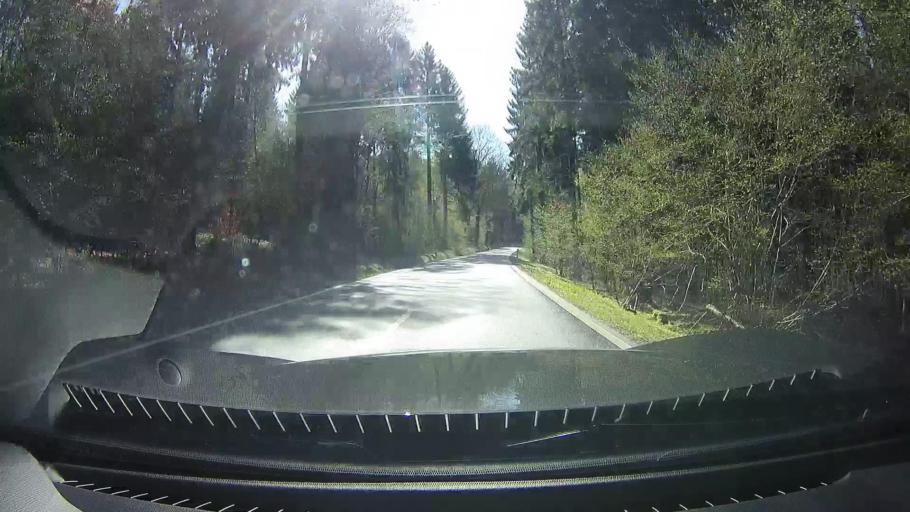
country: DE
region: Baden-Wuerttemberg
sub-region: Karlsruhe Region
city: Eberbach
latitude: 49.4260
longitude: 8.9777
